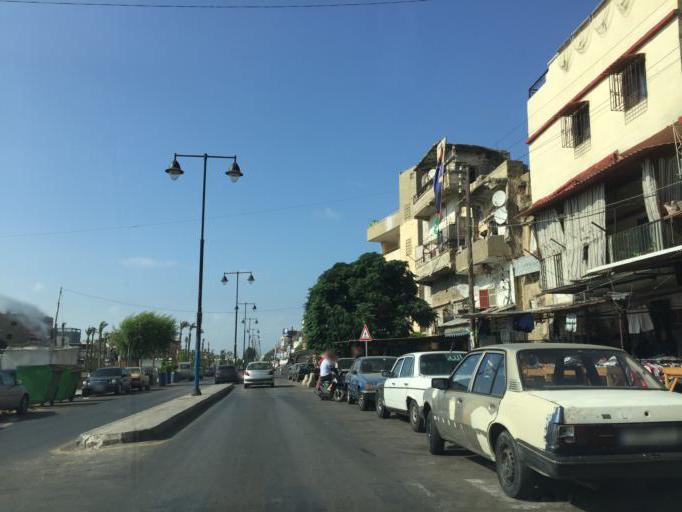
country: LB
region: Liban-Nord
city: Tripoli
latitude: 34.4361
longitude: 35.8469
